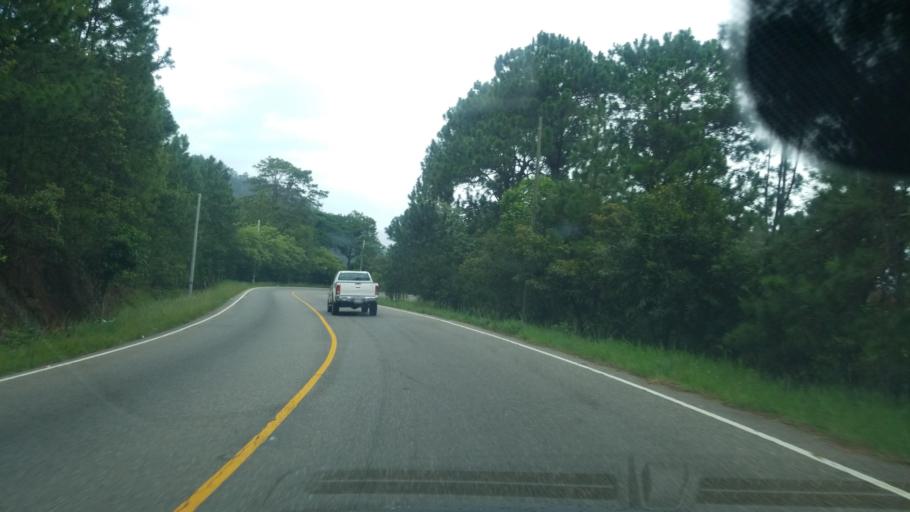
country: HN
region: Ocotepeque
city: Sinuapa
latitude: 14.4613
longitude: -89.1591
